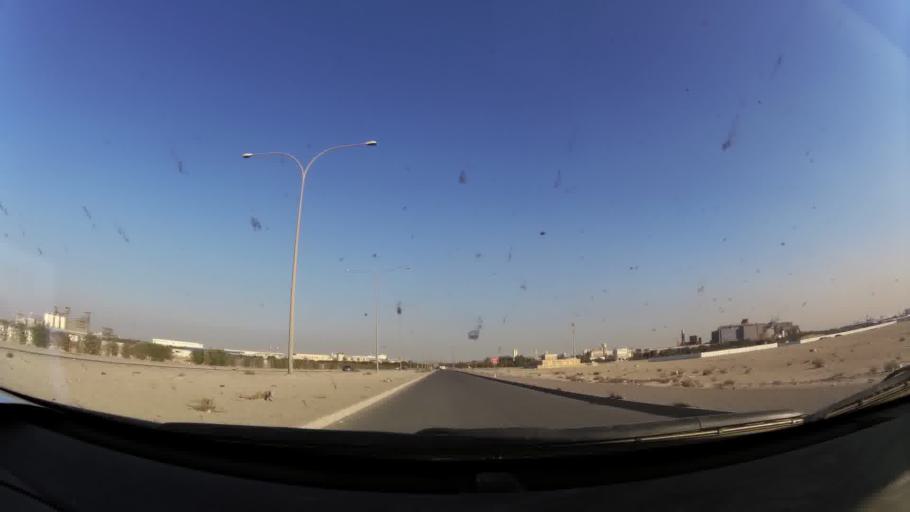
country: KW
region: Al Ahmadi
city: Al Fahahil
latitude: 28.9953
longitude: 48.1210
